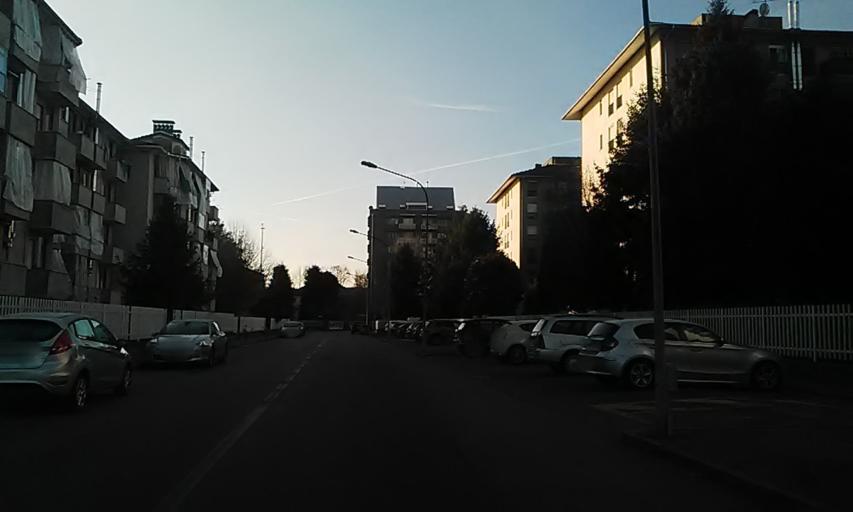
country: IT
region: Piedmont
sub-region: Provincia di Vercelli
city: Vercelli
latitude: 45.3209
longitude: 8.4038
